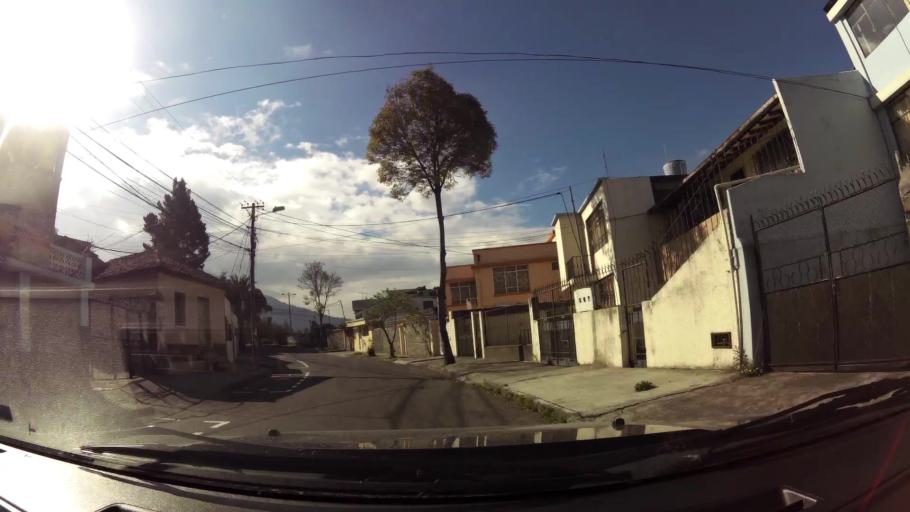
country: EC
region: Pichincha
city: Quito
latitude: -0.2156
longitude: -78.4923
